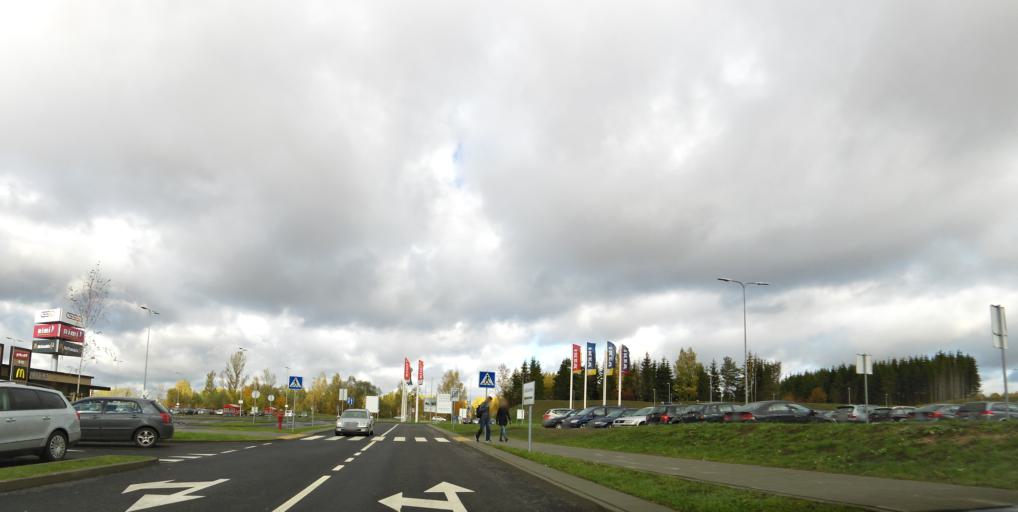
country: LT
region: Vilnius County
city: Naujamiestis
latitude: 54.6524
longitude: 25.2789
